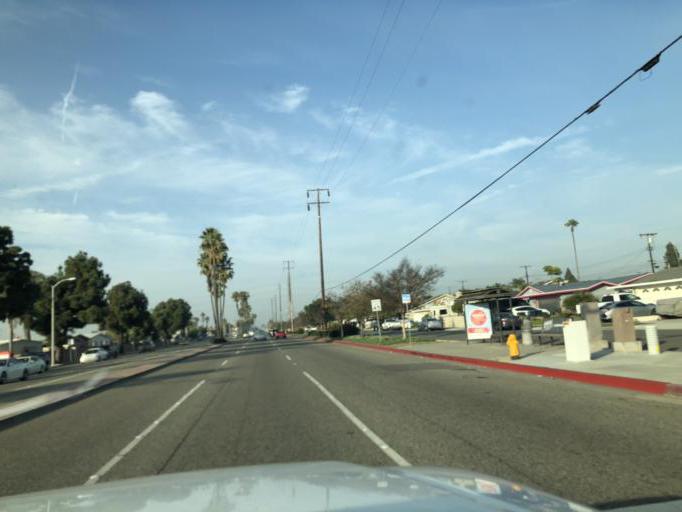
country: US
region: California
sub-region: Orange County
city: Fountain Valley
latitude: 33.6798
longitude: -117.9539
